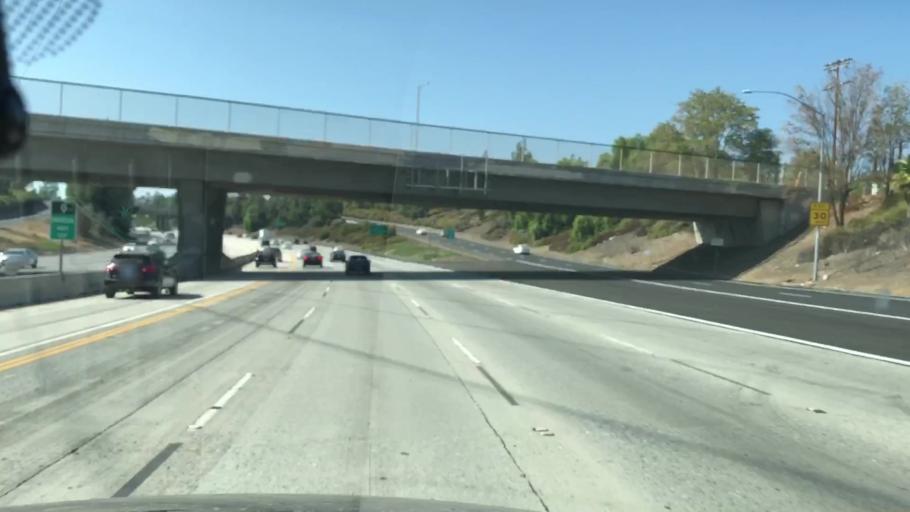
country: US
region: California
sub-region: Los Angeles County
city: San Fernando
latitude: 34.2773
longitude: -118.4974
